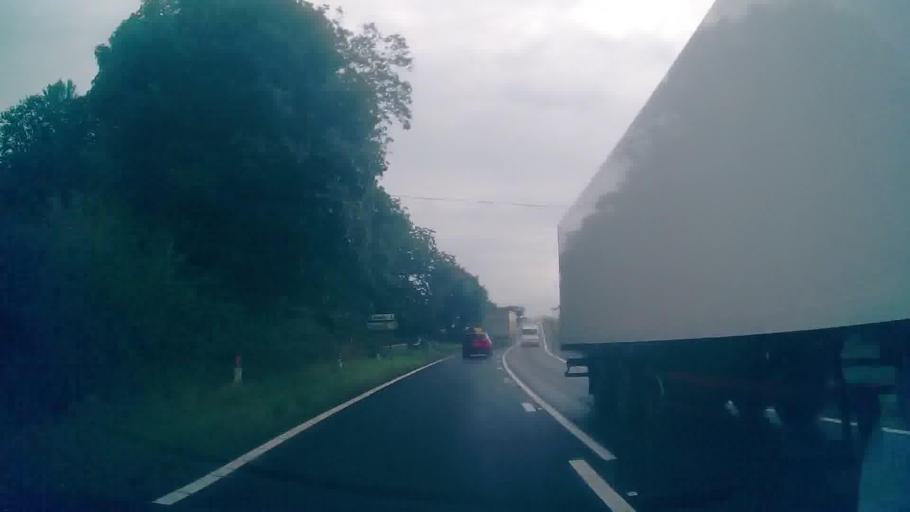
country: GB
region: Scotland
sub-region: Dumfries and Galloway
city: Lochmaben
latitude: 55.0527
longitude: -3.4644
